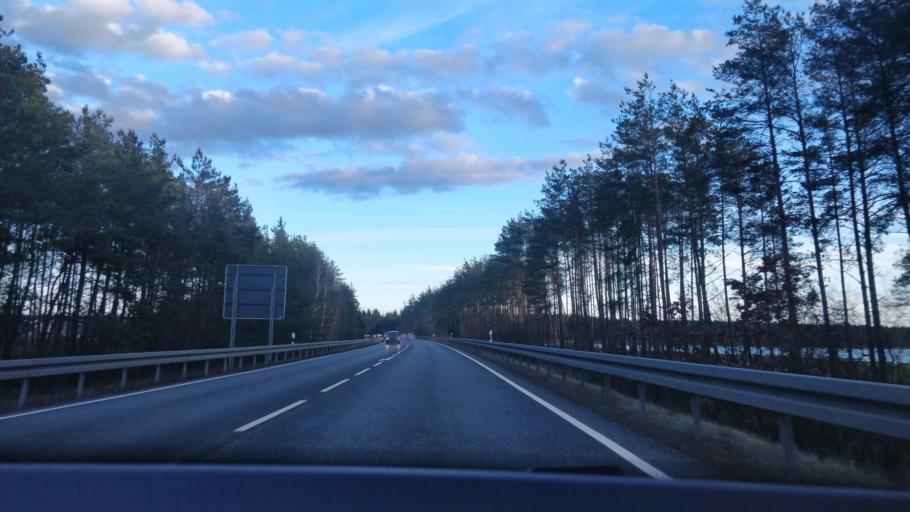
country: DE
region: Bavaria
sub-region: Upper Palatinate
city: Schwarzenbach
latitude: 49.7239
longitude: 11.9700
